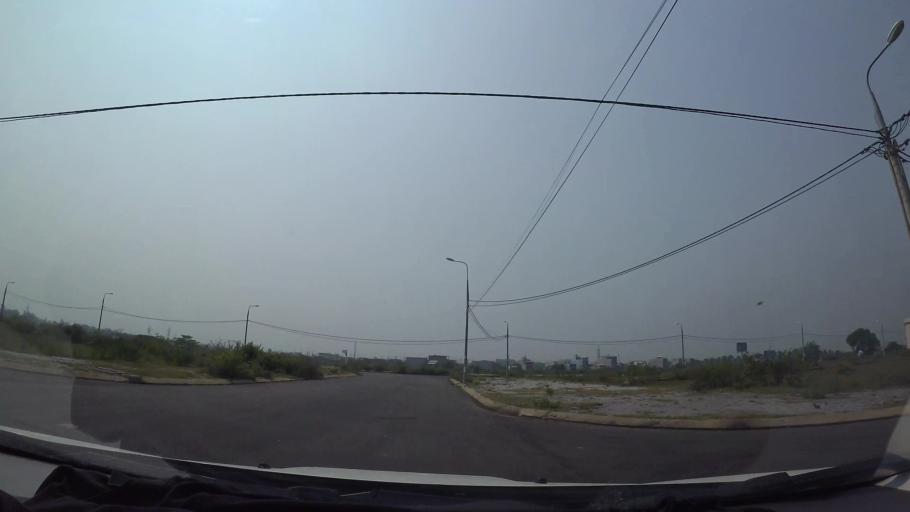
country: VN
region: Da Nang
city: Cam Le
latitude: 15.9743
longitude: 108.2125
